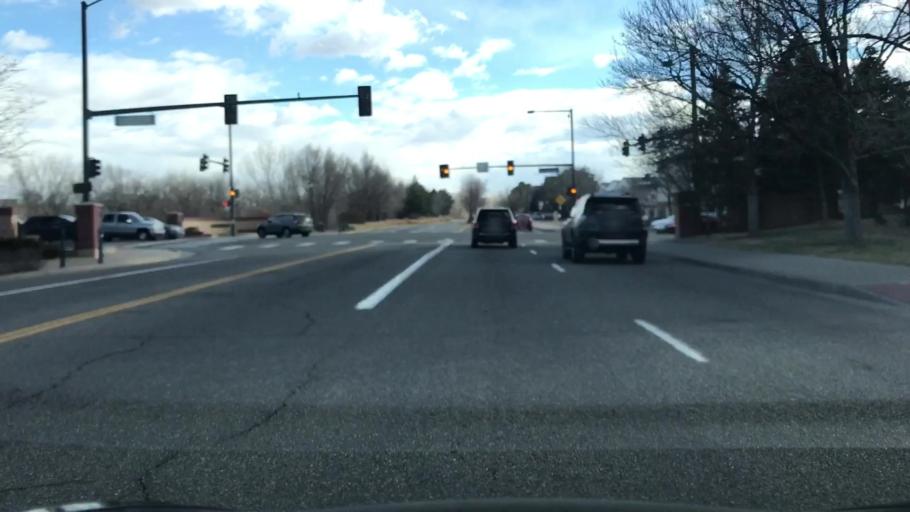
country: US
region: Colorado
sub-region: Arapahoe County
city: Glendale
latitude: 39.7044
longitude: -104.9347
